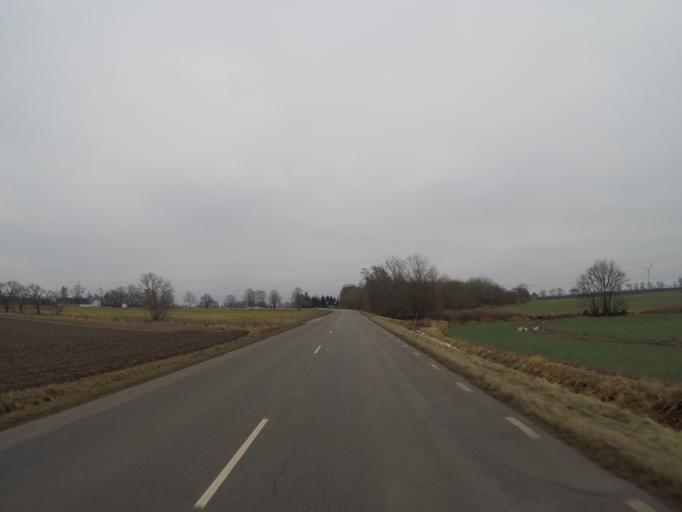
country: SE
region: Skane
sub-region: Hoors Kommun
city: Loberod
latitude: 55.7710
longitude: 13.4401
